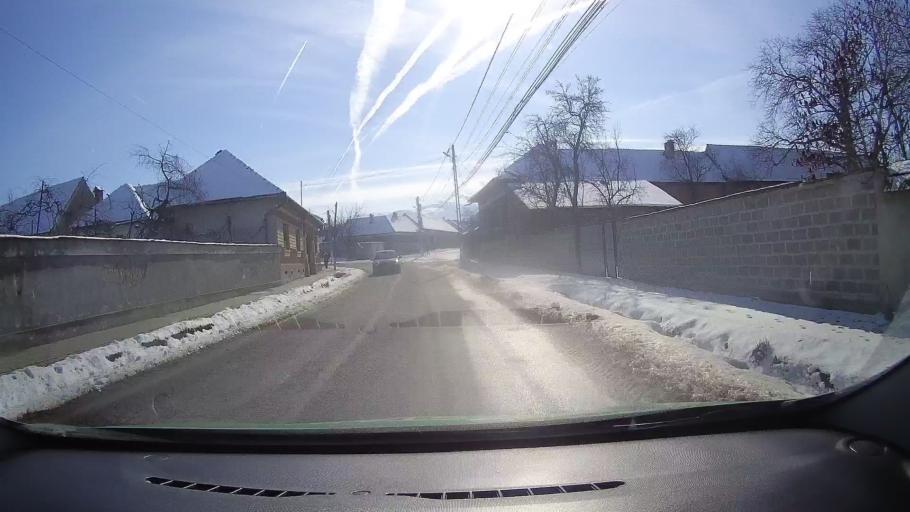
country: RO
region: Brasov
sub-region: Comuna Lisa
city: Lisa
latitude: 45.7253
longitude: 24.8516
